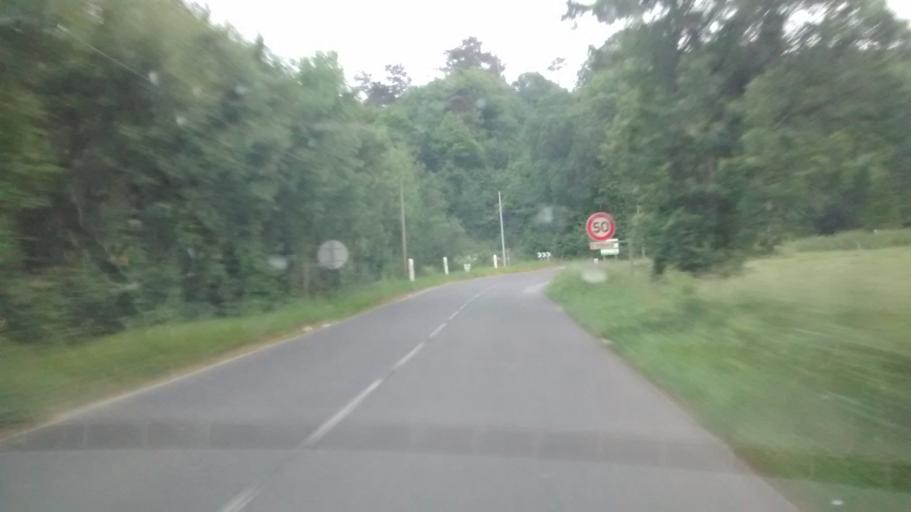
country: FR
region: Brittany
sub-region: Departement du Morbihan
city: Saint-Martin-sur-Oust
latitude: 47.7410
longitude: -2.2689
